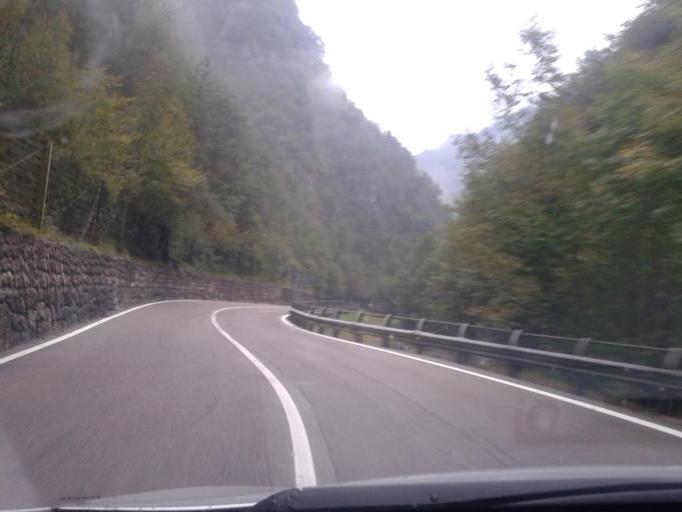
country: IT
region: Trentino-Alto Adige
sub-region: Provincia di Trento
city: Storo
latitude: 45.8446
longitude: 10.6092
